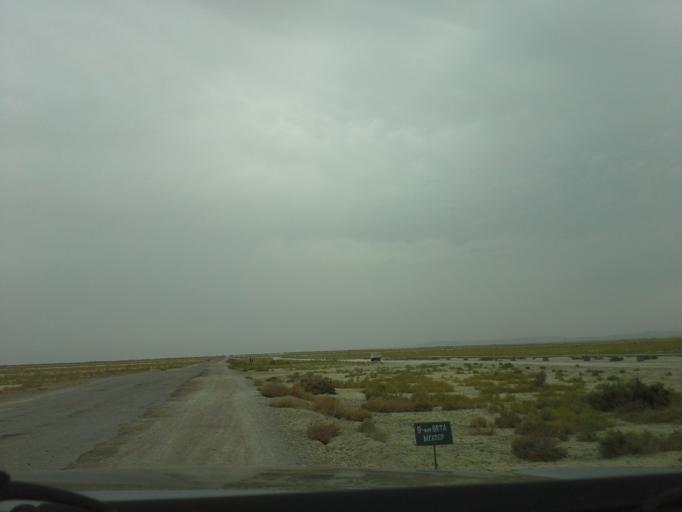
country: TM
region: Lebap
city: Atamyrat
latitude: 37.7437
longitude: 65.4821
